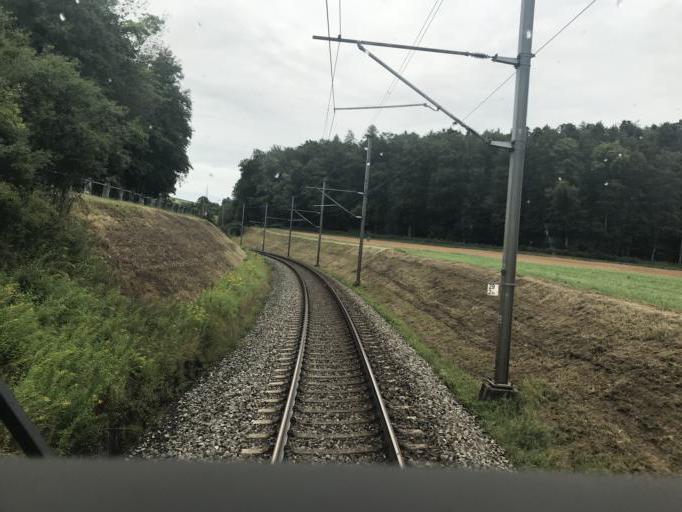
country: DE
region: Baden-Wuerttemberg
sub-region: Freiburg Region
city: Lottstetten
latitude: 47.6194
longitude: 8.5608
